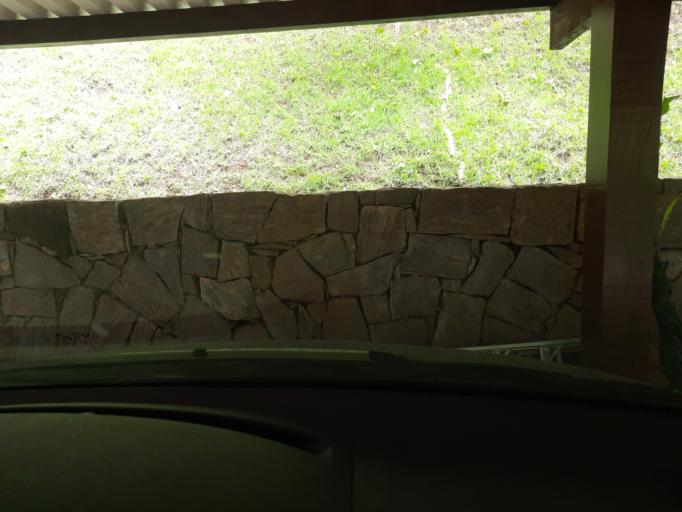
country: BR
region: Rio de Janeiro
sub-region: Petropolis
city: Petropolis
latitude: -22.4424
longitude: -43.1733
